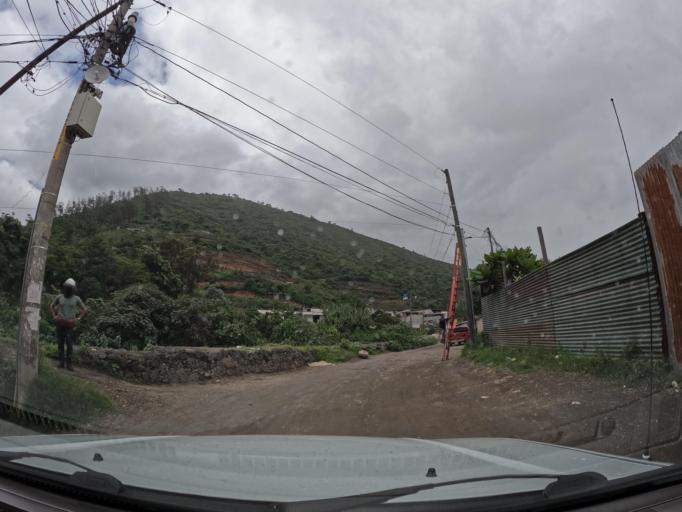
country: GT
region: Sacatepequez
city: Jocotenango
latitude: 14.5818
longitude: -90.7483
